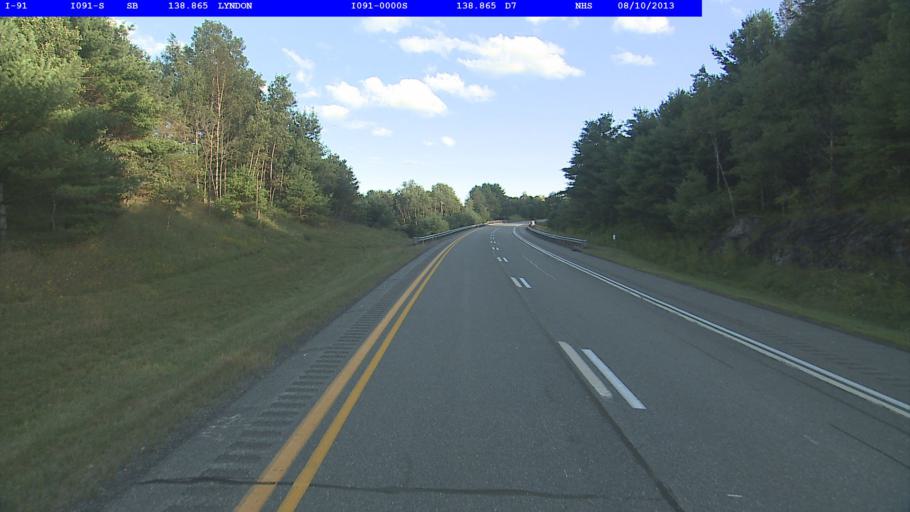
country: US
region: Vermont
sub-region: Caledonia County
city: Lyndonville
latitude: 44.5401
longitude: -72.0206
